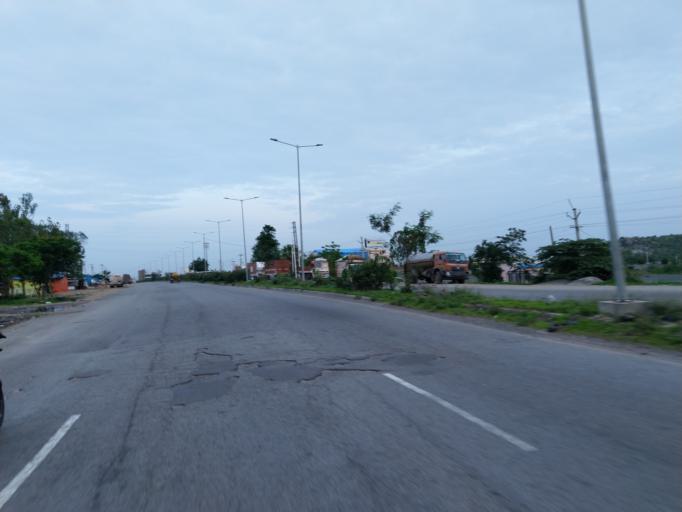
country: IN
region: Telangana
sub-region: Rangareddi
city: Lal Bahadur Nagar
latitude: 17.3170
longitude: 78.6666
